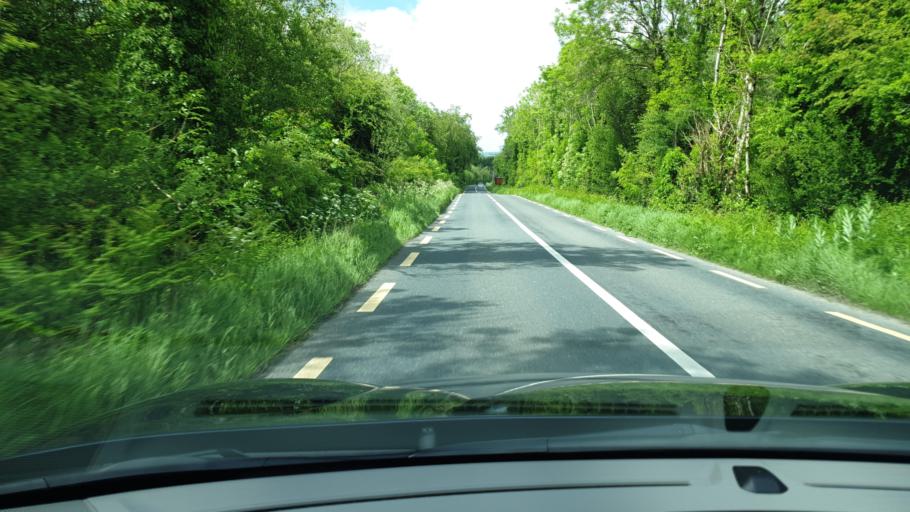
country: IE
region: Ulster
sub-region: An Cabhan
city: Kingscourt
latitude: 53.8947
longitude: -6.7607
